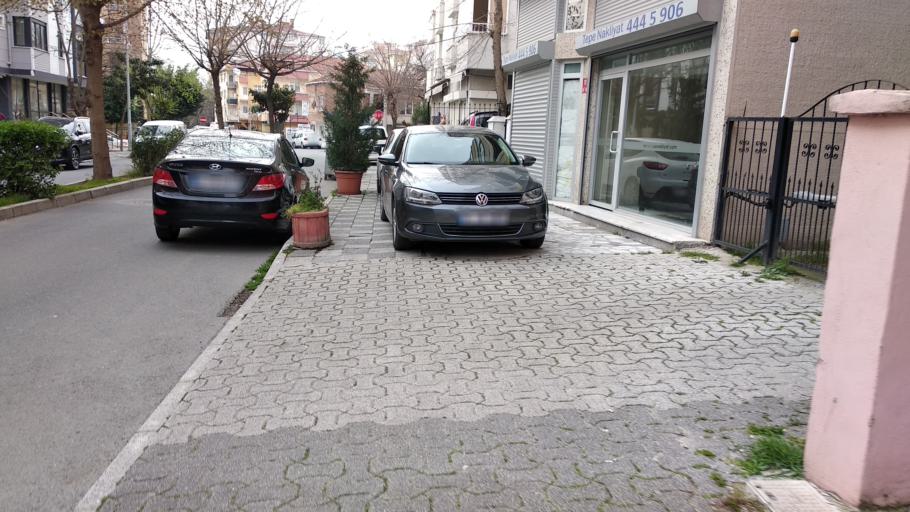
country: TR
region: Istanbul
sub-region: Atasehir
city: Atasehir
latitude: 40.9717
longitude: 29.1146
